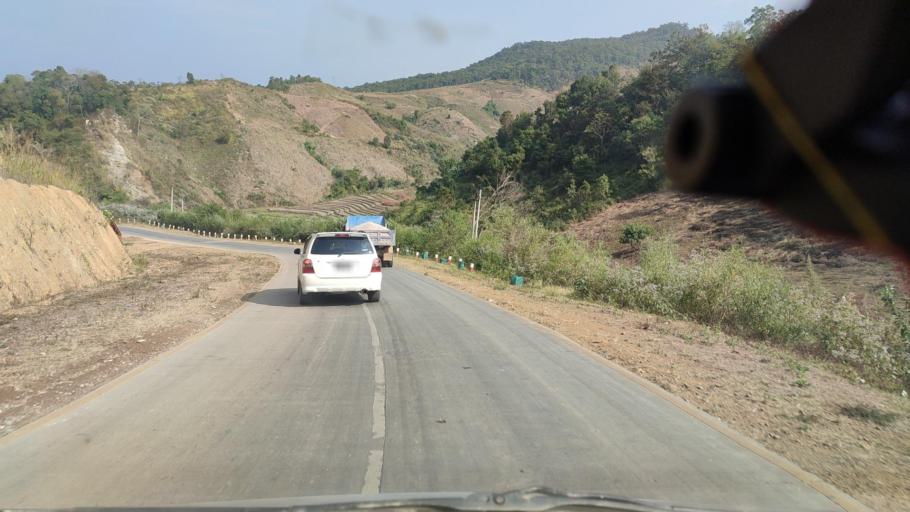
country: CN
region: Yunnan
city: Nayun
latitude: 21.7861
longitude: 99.5155
